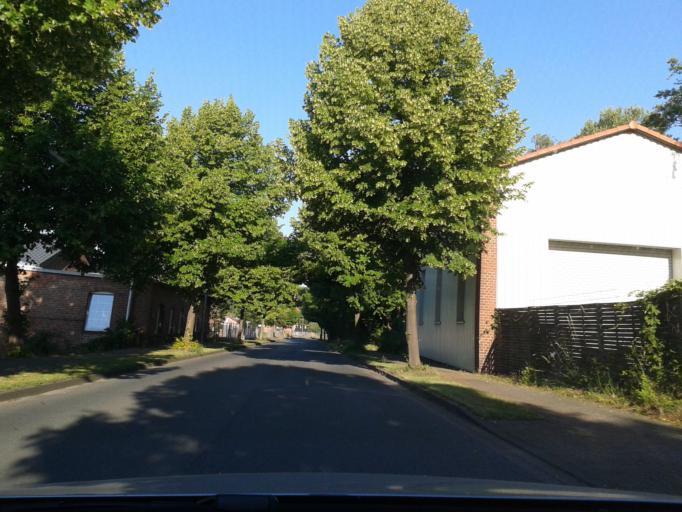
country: DE
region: North Rhine-Westphalia
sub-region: Regierungsbezirk Detmold
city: Dorentrup
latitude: 52.0350
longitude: 8.9941
